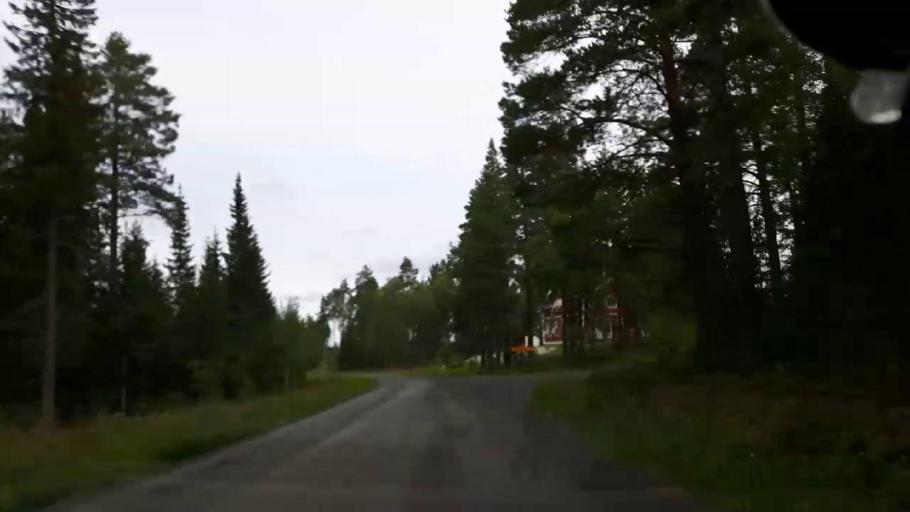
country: SE
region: Jaemtland
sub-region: Krokoms Kommun
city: Krokom
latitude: 63.3116
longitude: 14.3202
